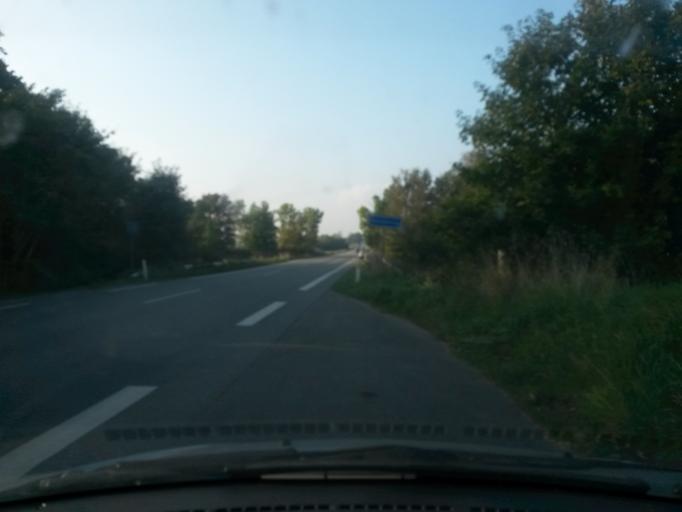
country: DK
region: Central Jutland
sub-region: Syddjurs Kommune
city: Hornslet
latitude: 56.3612
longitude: 10.3332
